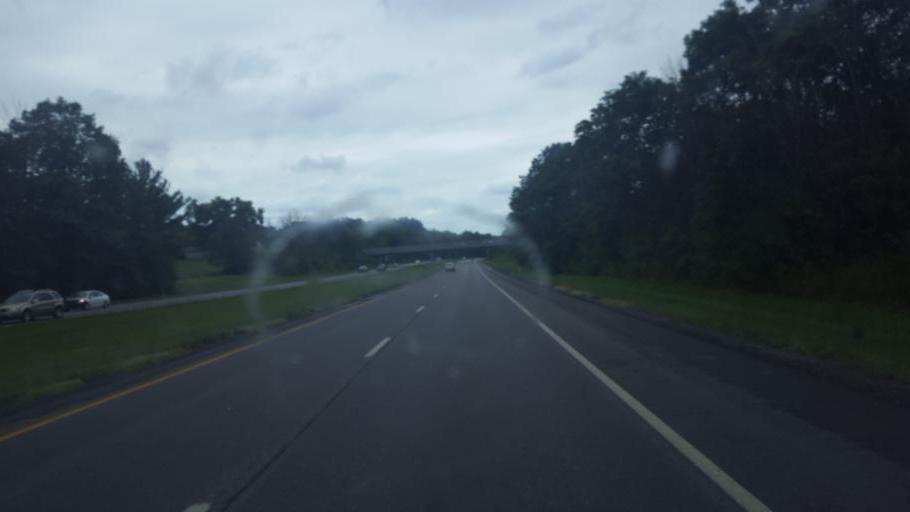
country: US
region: Ohio
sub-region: Lake County
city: Painesville
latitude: 41.6770
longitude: -81.2514
